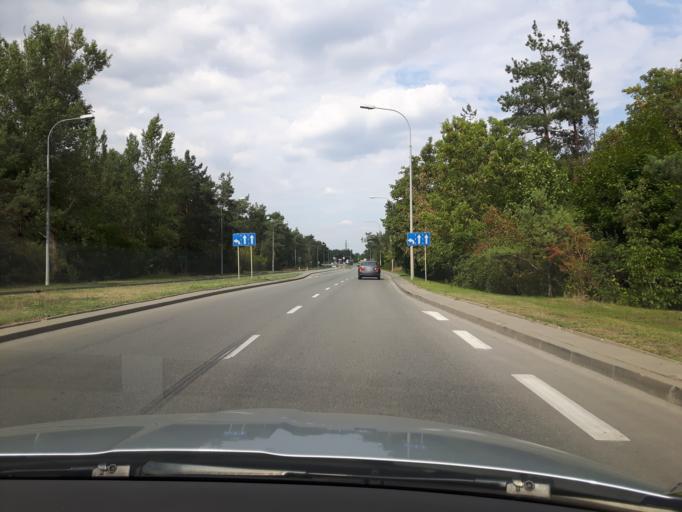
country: PL
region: Masovian Voivodeship
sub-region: Warszawa
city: Targowek
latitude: 52.3242
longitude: 21.0275
